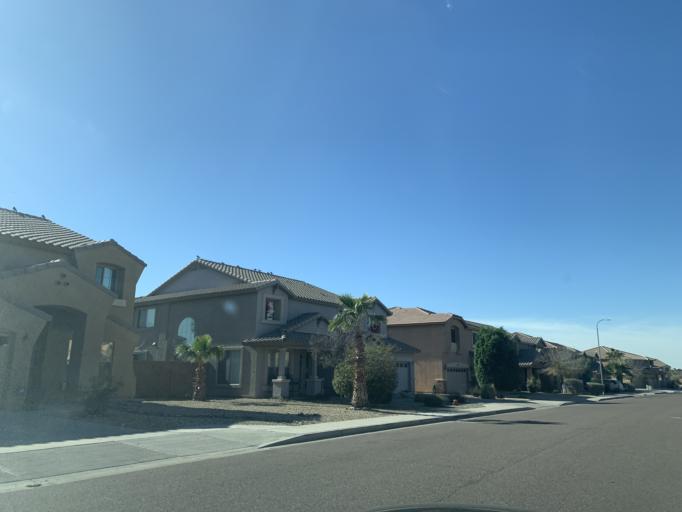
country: US
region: Arizona
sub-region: Maricopa County
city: Laveen
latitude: 33.3906
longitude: -112.1283
